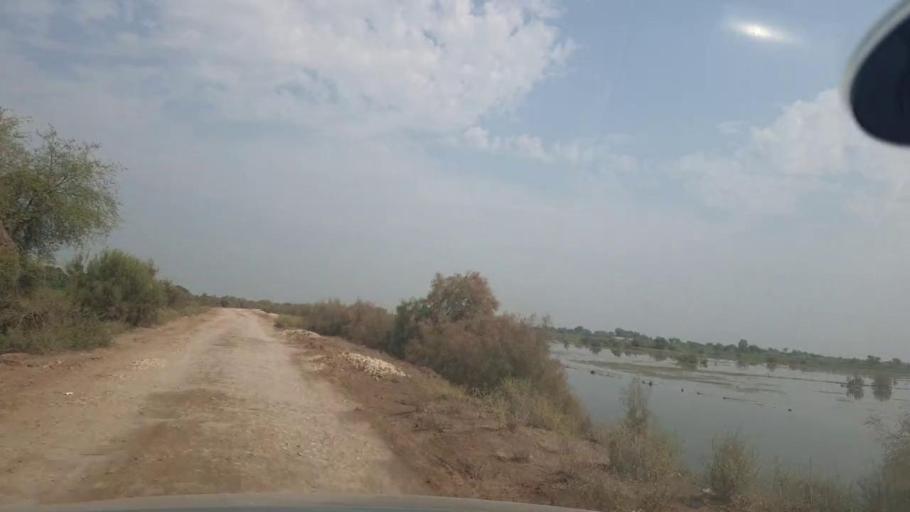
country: PK
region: Balochistan
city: Mehrabpur
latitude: 28.1100
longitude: 68.0903
